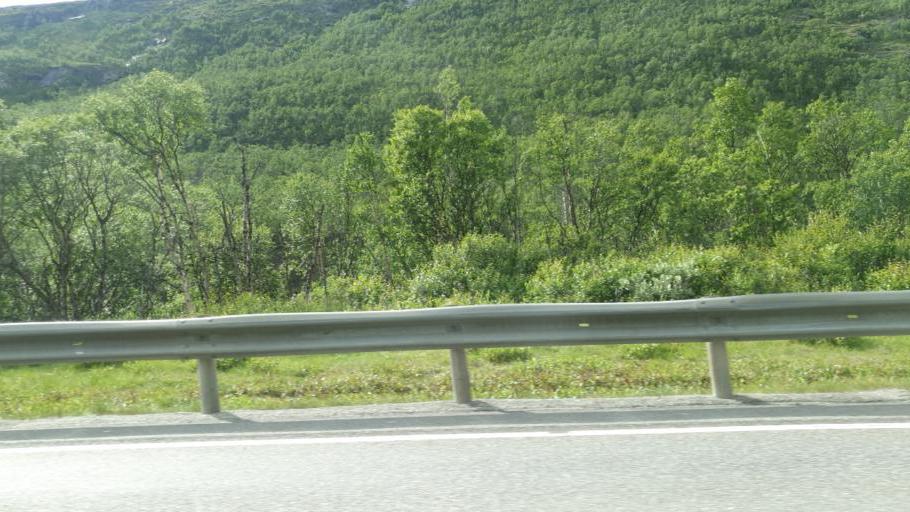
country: NO
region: Sor-Trondelag
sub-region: Oppdal
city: Oppdal
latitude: 62.3243
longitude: 9.6214
